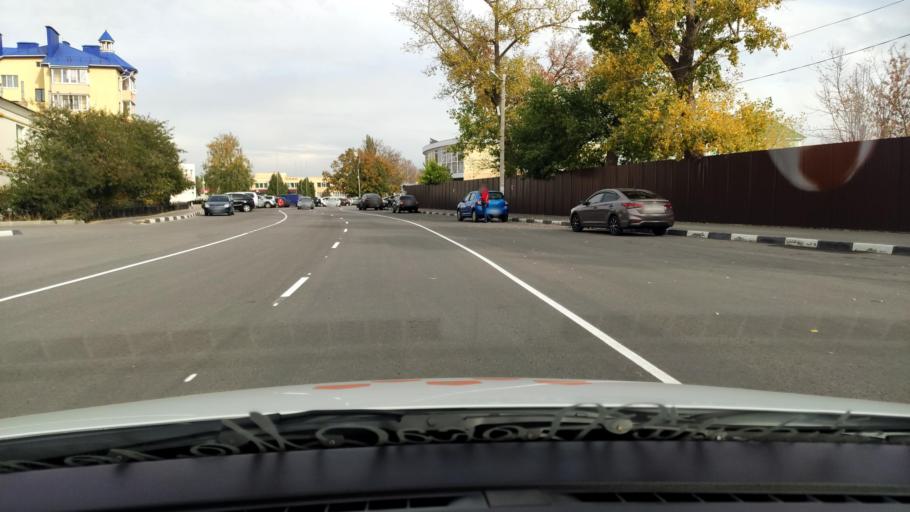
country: RU
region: Voronezj
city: Ramon'
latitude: 51.9109
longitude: 39.3383
